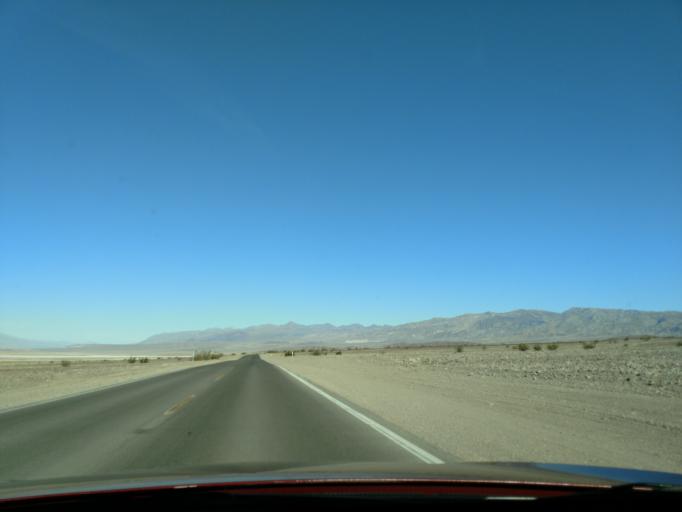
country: US
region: Nevada
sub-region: Nye County
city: Beatty
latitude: 36.5074
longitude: -116.8787
